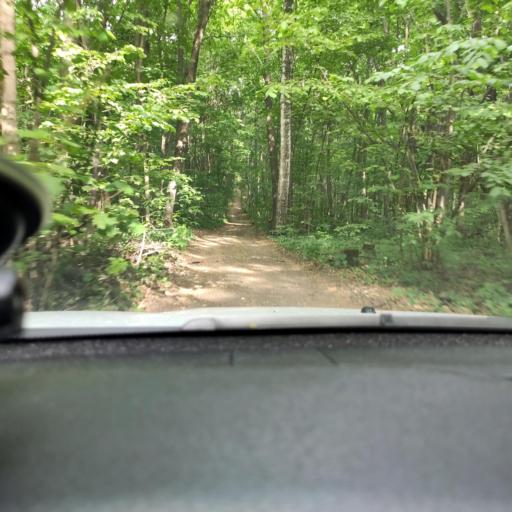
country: RU
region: Samara
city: Samara
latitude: 53.3176
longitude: 50.2138
